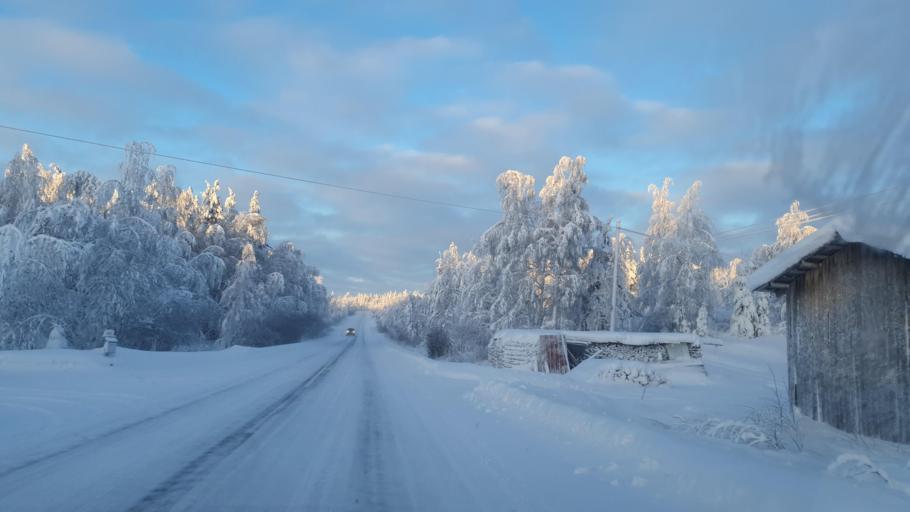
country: FI
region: Kainuu
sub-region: Kajaani
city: Vuokatti
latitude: 64.2666
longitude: 28.2432
